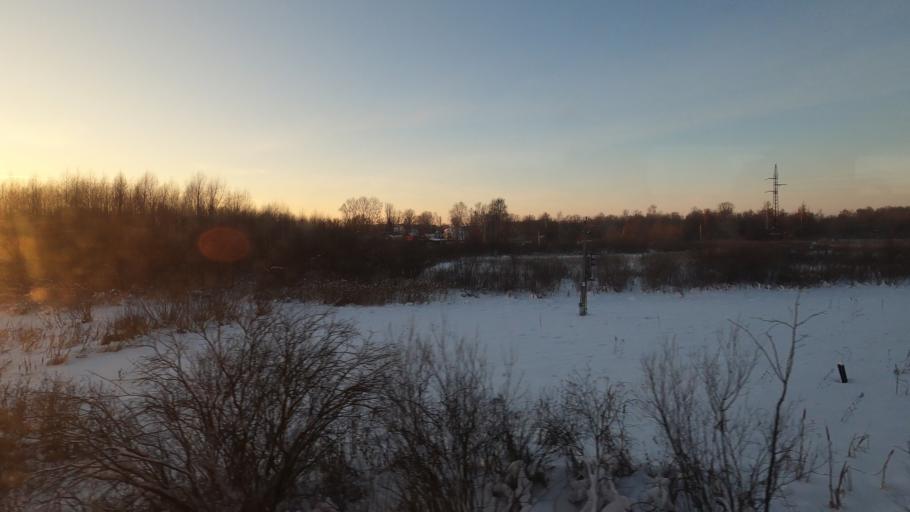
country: RU
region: Moskovskaya
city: Dmitrov
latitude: 56.3563
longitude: 37.5201
